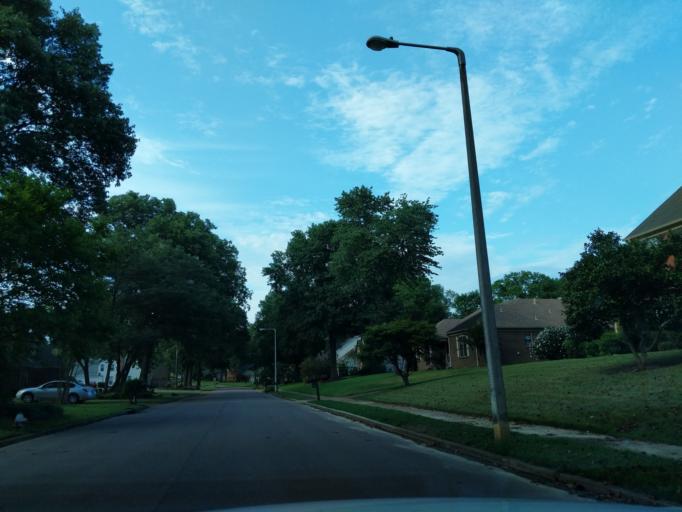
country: US
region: Tennessee
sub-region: Shelby County
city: Germantown
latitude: 35.0646
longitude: -89.7845
